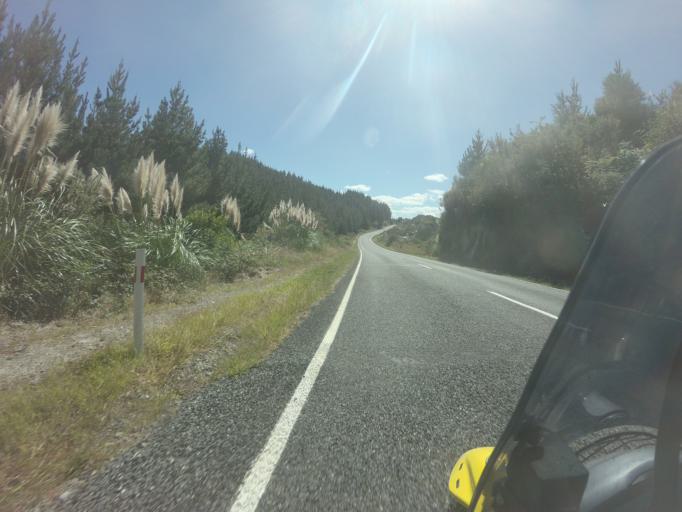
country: NZ
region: Bay of Plenty
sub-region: Kawerau District
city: Kawerau
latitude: -38.2810
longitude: 176.8163
